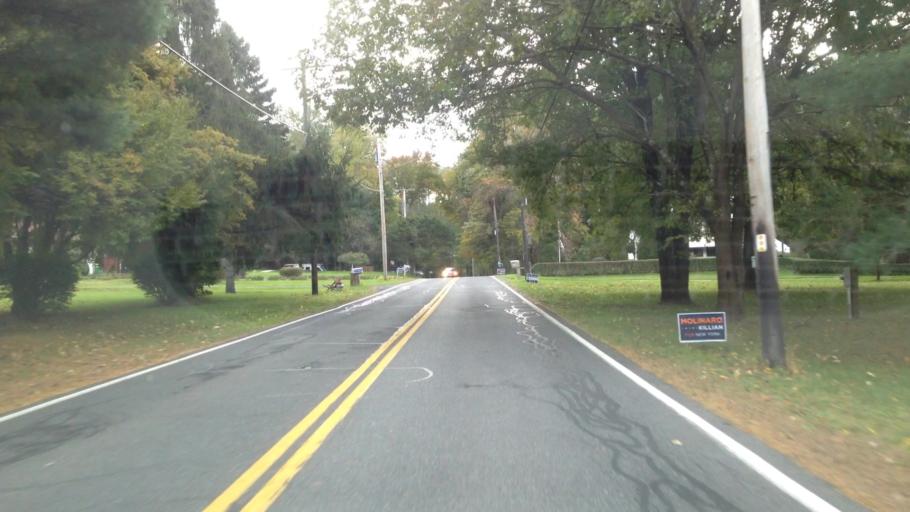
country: US
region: New York
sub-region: Ulster County
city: Tillson
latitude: 41.8366
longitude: -74.0801
